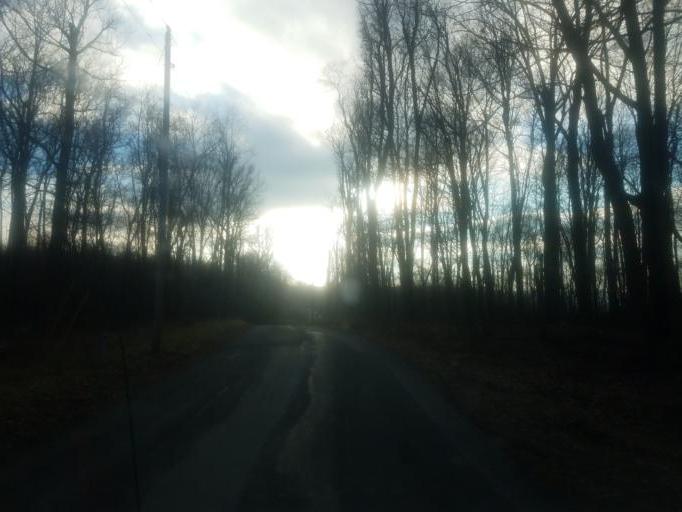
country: US
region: Ohio
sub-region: Ashland County
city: Loudonville
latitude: 40.6083
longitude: -82.3703
